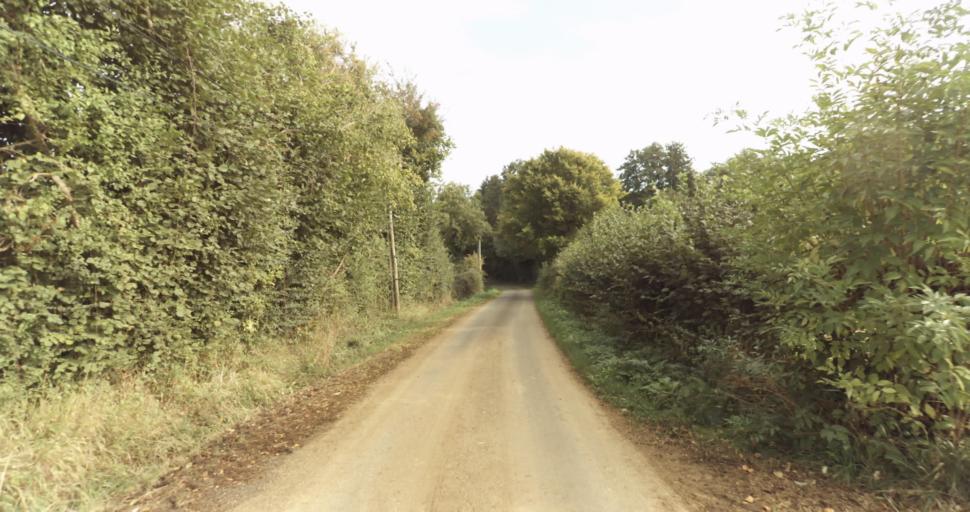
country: FR
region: Lower Normandy
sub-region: Departement de l'Orne
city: Vimoutiers
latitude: 48.8519
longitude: 0.2218
